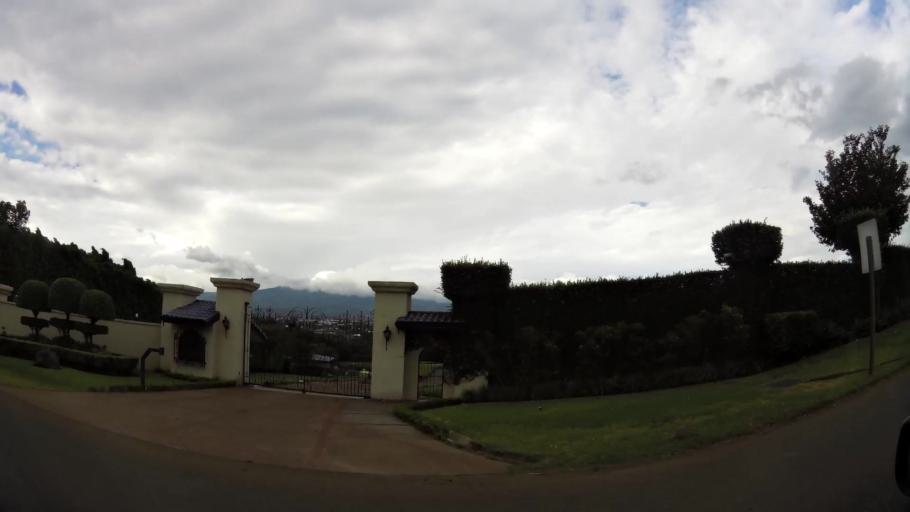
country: CR
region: Heredia
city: La Asuncion
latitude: 9.9553
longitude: -84.1681
